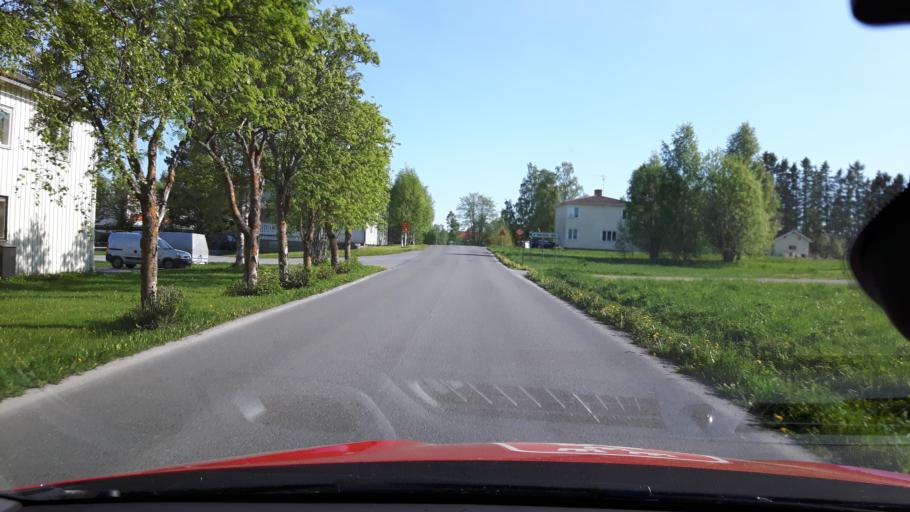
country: SE
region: Jaemtland
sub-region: Bergs Kommun
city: Hoverberg
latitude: 62.9246
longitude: 14.5160
